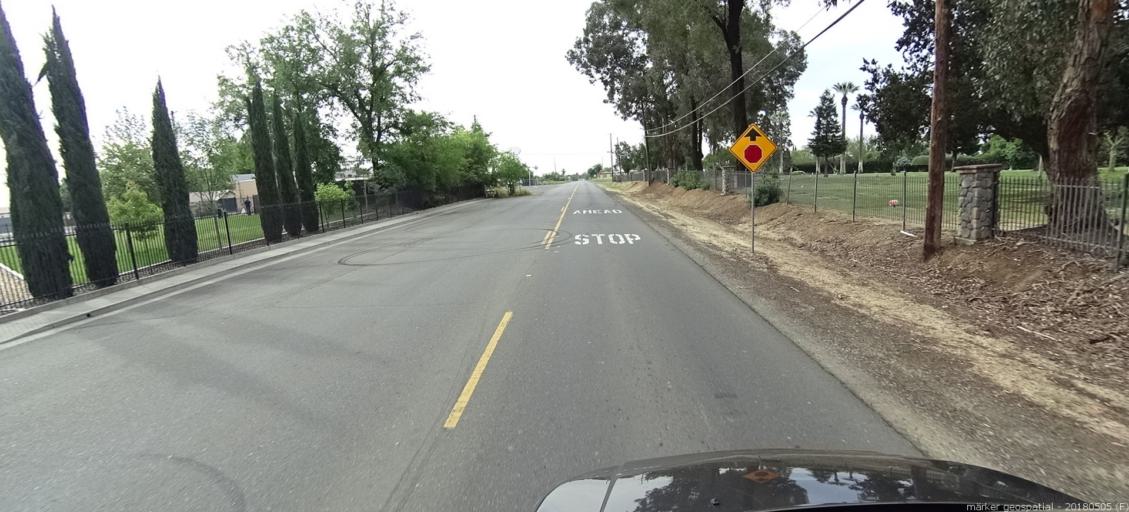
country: US
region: California
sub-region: Sacramento County
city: Rio Linda
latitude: 38.6529
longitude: -121.4394
